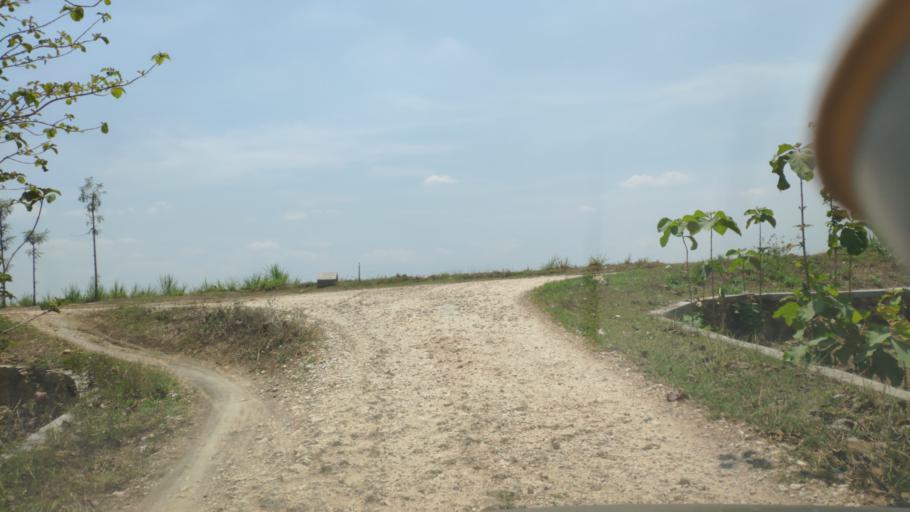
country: ID
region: Central Java
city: Gesik
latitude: -7.0438
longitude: 111.3254
